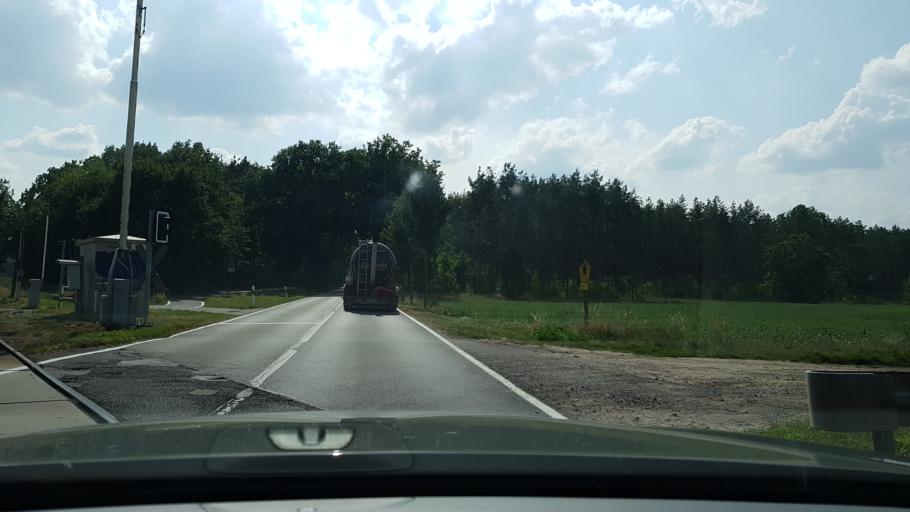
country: DE
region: Brandenburg
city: Lindow
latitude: 52.9493
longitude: 12.9761
